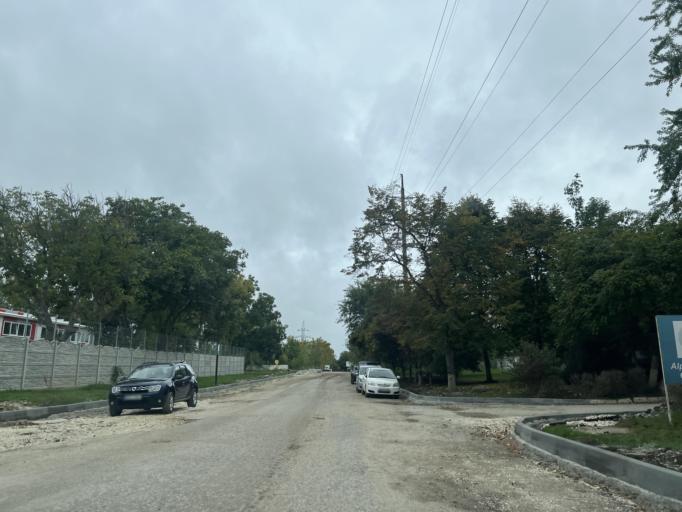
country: MD
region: Ungheni
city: Ungheni
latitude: 47.2245
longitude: 27.8066
